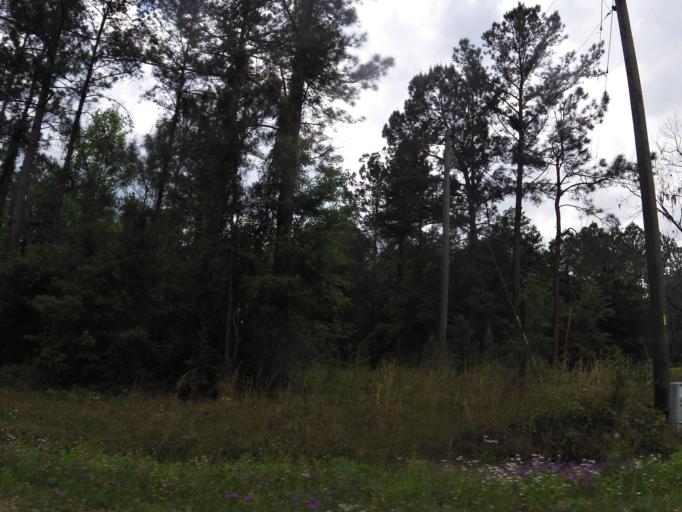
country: US
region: Georgia
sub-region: Charlton County
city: Folkston
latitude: 30.8090
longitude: -82.0626
